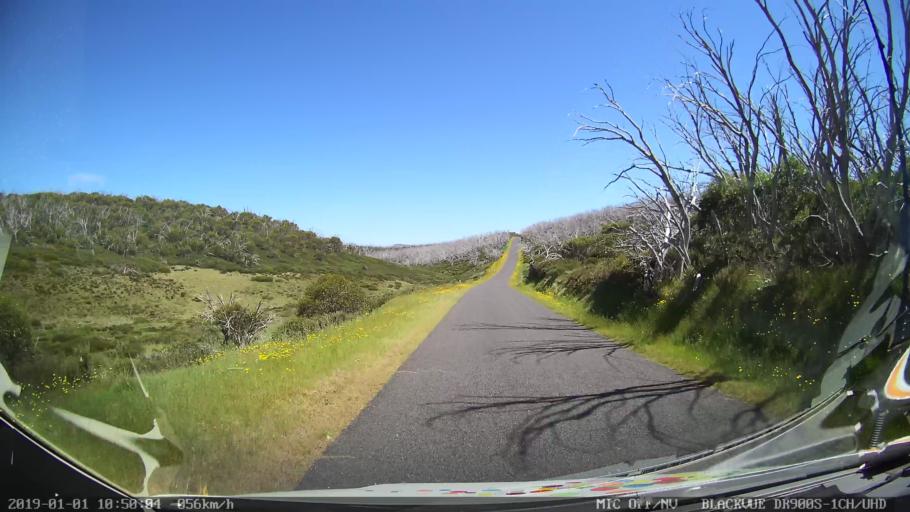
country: AU
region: New South Wales
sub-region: Snowy River
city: Jindabyne
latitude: -36.0316
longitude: 148.3734
